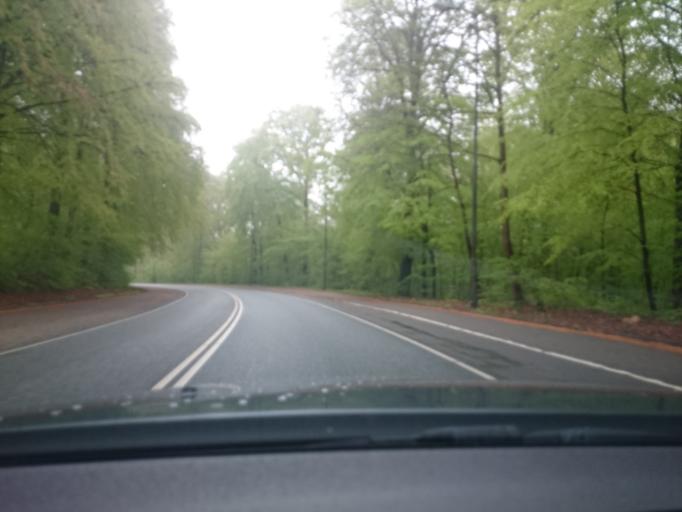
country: DK
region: Capital Region
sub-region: Lyngby-Tarbaek Kommune
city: Kongens Lyngby
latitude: 55.7726
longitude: 12.5489
